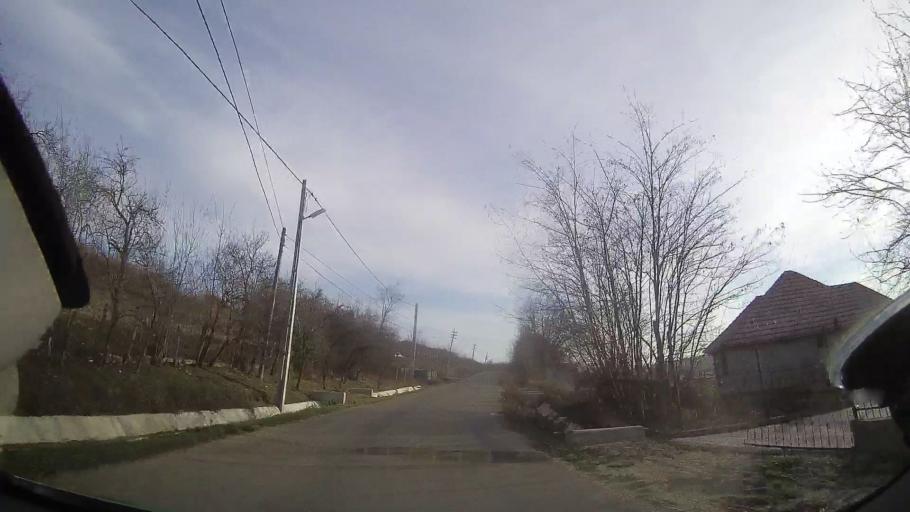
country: RO
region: Bihor
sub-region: Comuna Sarbi
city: Sarbi
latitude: 47.1889
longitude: 22.1256
